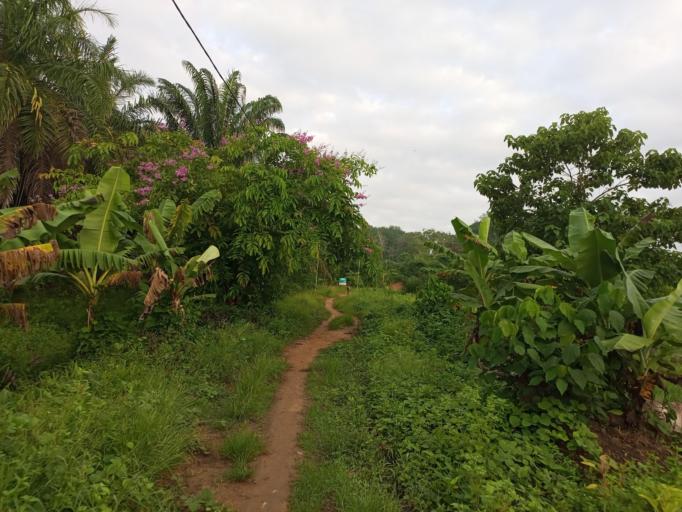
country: SL
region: Eastern Province
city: Pendembu
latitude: 8.1037
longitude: -10.6963
